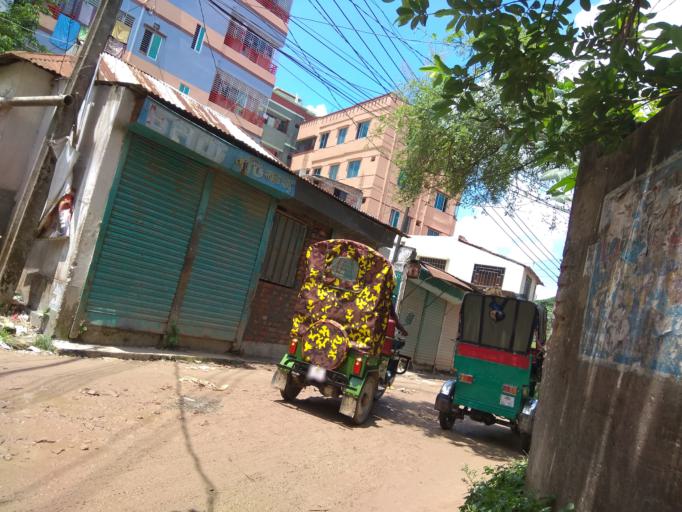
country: BD
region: Dhaka
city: Tungi
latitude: 23.8286
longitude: 90.3896
